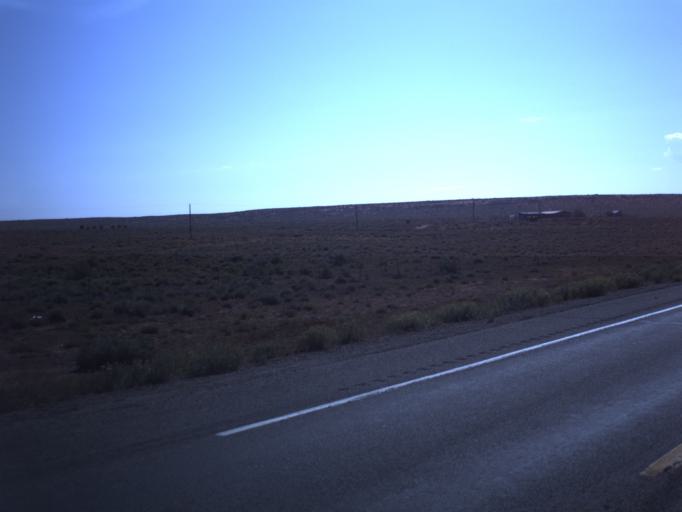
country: US
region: Utah
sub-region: San Juan County
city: Blanding
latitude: 37.1715
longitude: -109.5808
